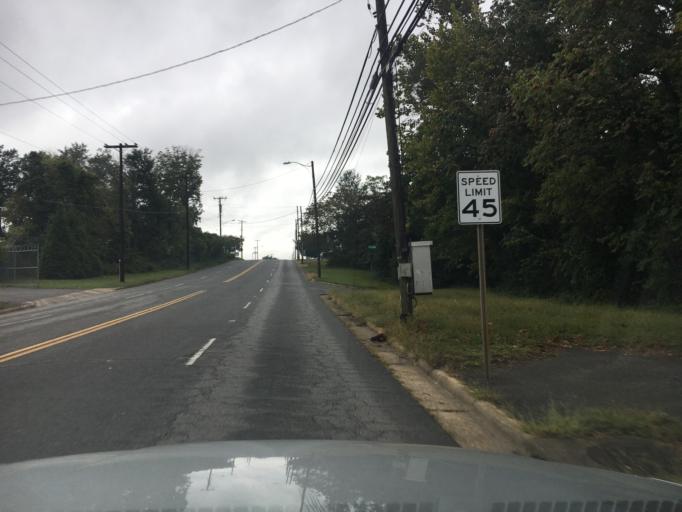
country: US
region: North Carolina
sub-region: Catawba County
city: Hickory
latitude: 35.7379
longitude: -81.3560
